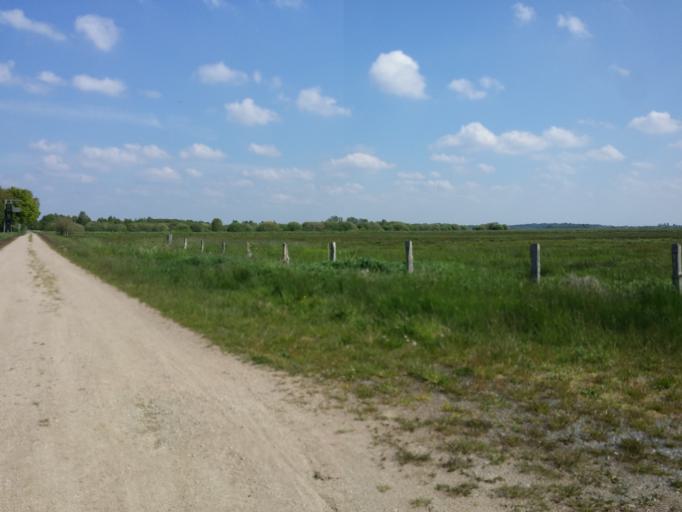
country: DE
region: Lower Saxony
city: Osterholz-Scharmbeck
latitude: 53.2302
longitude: 8.8432
